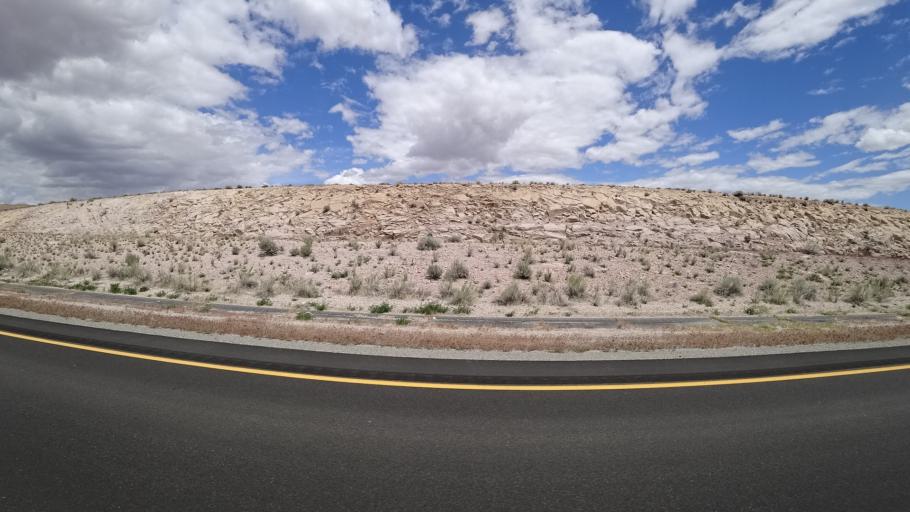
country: US
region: California
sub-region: Inyo County
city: West Bishop
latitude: 37.4420
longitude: -118.5720
